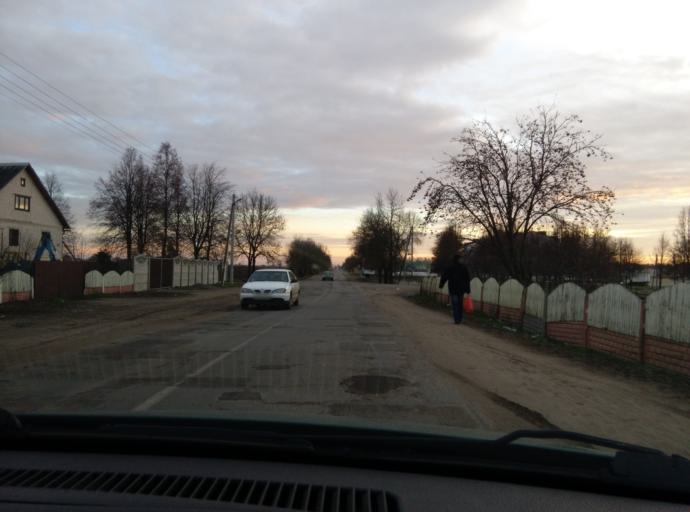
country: BY
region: Minsk
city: Horad Barysaw
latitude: 54.2807
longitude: 28.4942
